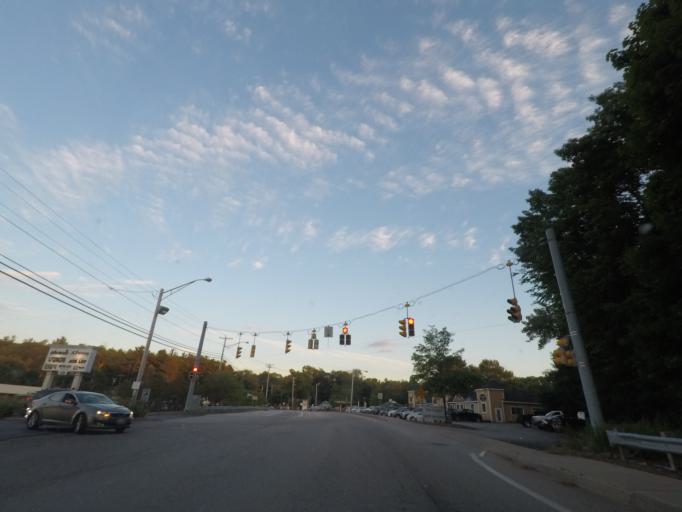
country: US
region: Massachusetts
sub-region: Worcester County
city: Sturbridge
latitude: 42.0972
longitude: -72.0726
